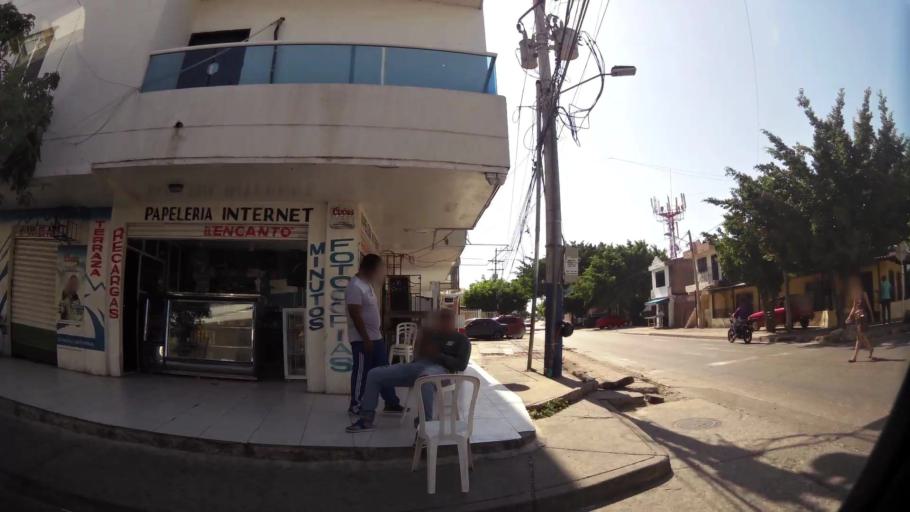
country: CO
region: Bolivar
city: Cartagena
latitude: 10.4093
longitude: -75.5186
